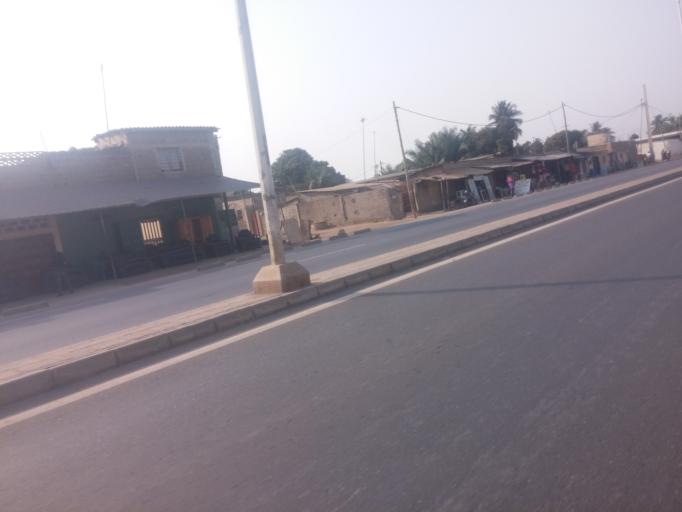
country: TG
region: Maritime
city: Lome
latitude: 6.1676
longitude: 1.2829
